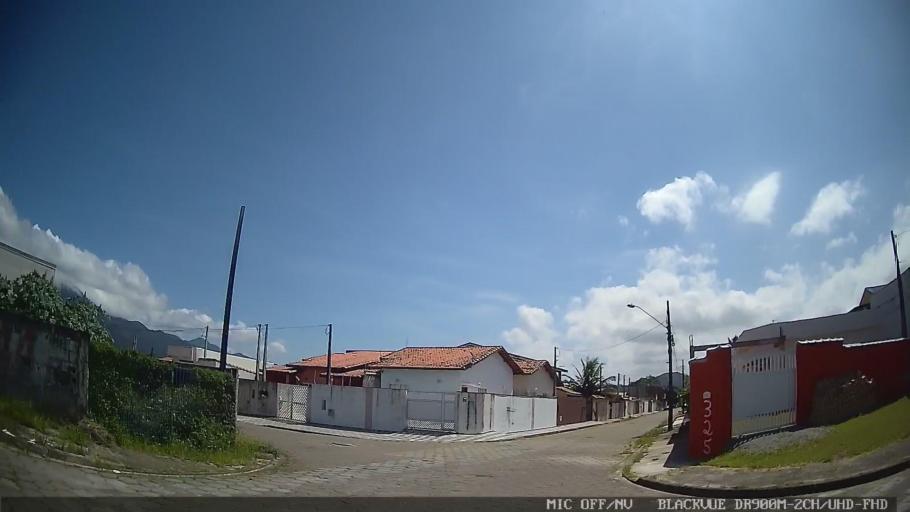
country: BR
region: Sao Paulo
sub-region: Peruibe
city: Peruibe
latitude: -24.3046
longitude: -47.0036
